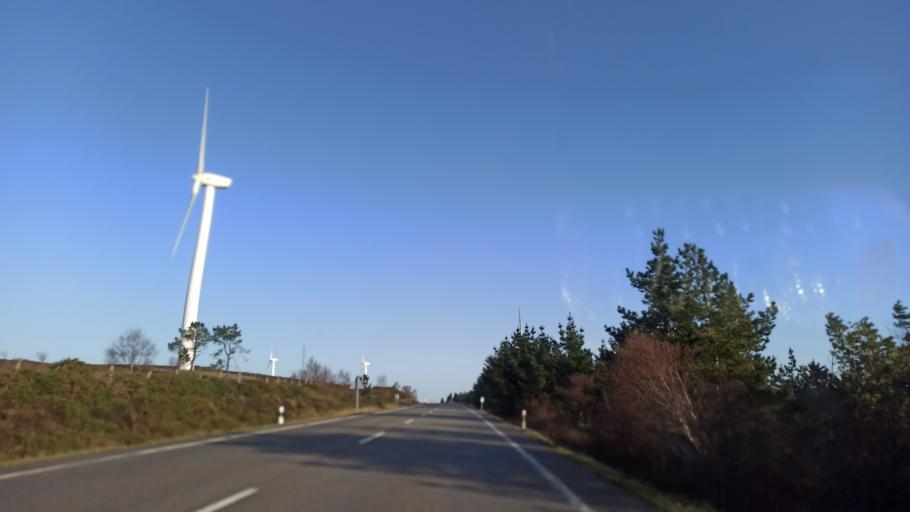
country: ES
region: Galicia
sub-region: Provincia da Coruna
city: As Pontes de Garcia Rodriguez
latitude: 43.5391
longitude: -7.8059
